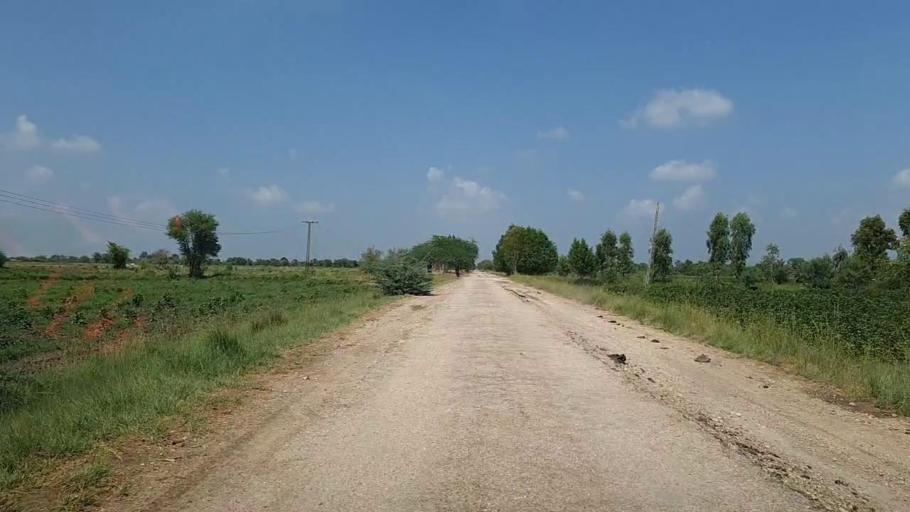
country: PK
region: Sindh
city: Kandiaro
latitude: 27.0160
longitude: 68.2673
